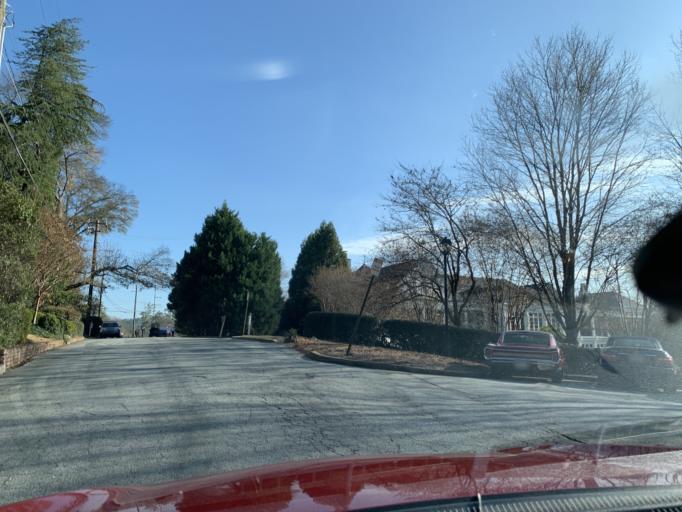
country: US
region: Georgia
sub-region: DeKalb County
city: Druid Hills
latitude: 33.8011
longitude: -84.3763
